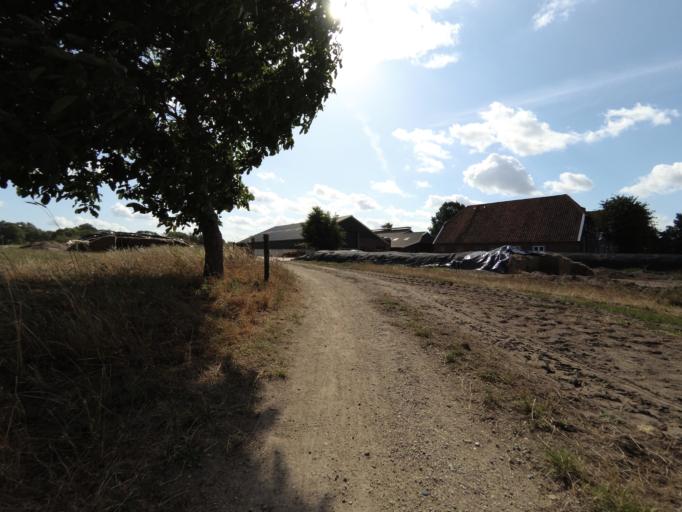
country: NL
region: Overijssel
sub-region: Gemeente Haaksbergen
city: Haaksbergen
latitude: 52.1491
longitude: 6.7610
